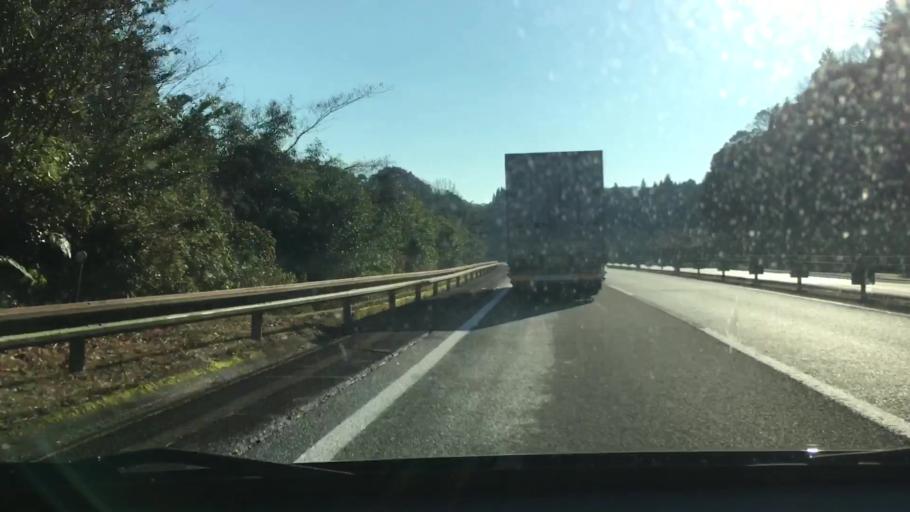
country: JP
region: Kagoshima
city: Kajiki
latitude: 31.8906
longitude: 130.6978
